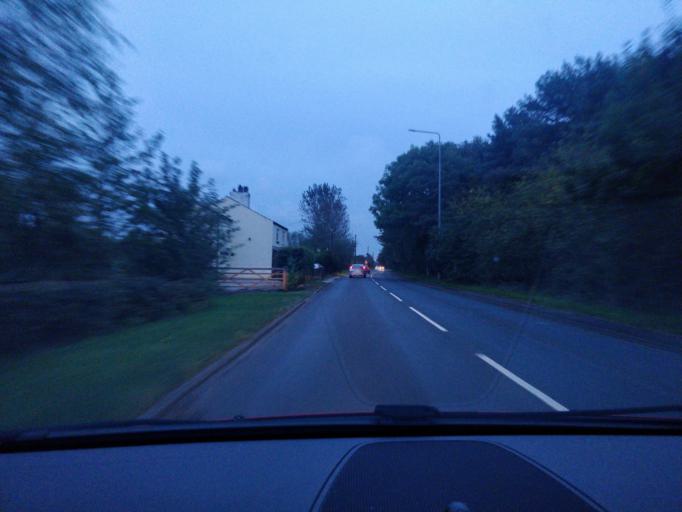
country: GB
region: England
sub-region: Lancashire
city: Ormskirk
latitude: 53.5833
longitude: -2.9058
